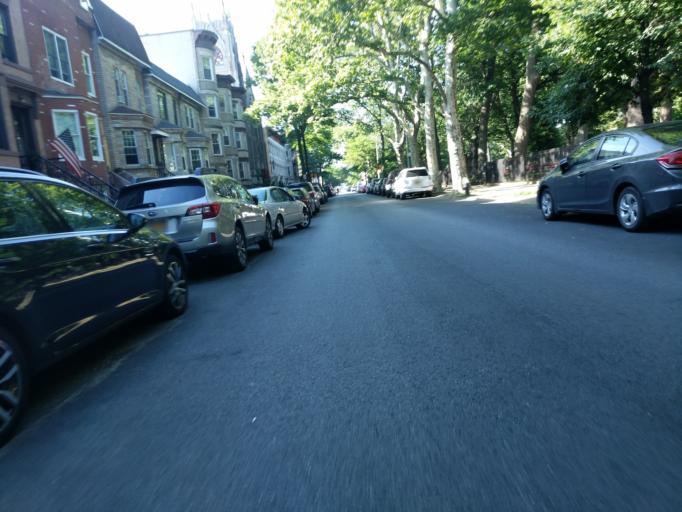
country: US
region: New York
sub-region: Queens County
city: Long Island City
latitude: 40.7241
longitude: -73.9442
